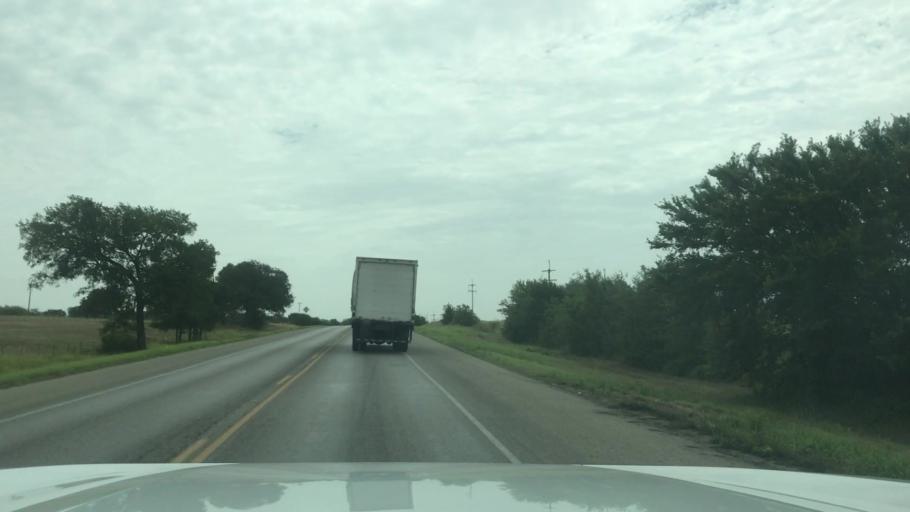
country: US
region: Texas
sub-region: Comanche County
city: De Leon
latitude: 32.0922
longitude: -98.4454
